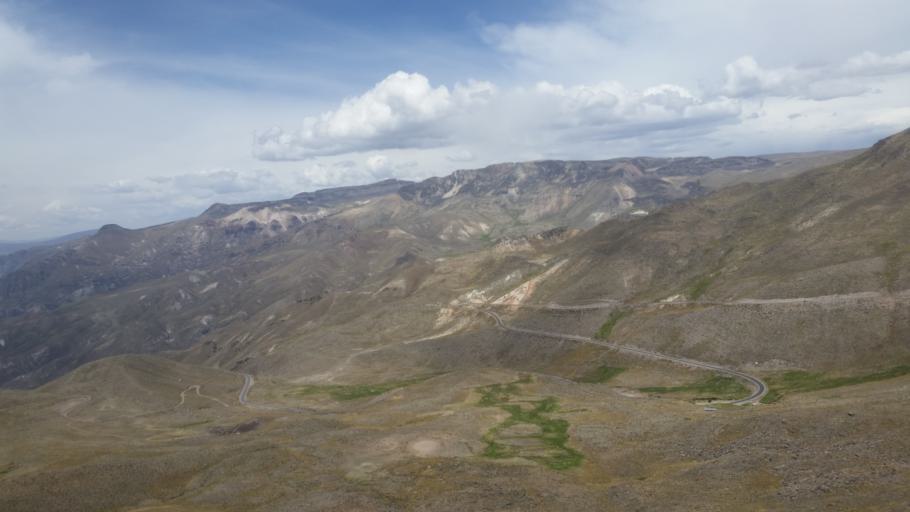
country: PE
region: Arequipa
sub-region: Provincia de Caylloma
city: Chivay
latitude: -15.7060
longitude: -71.6020
